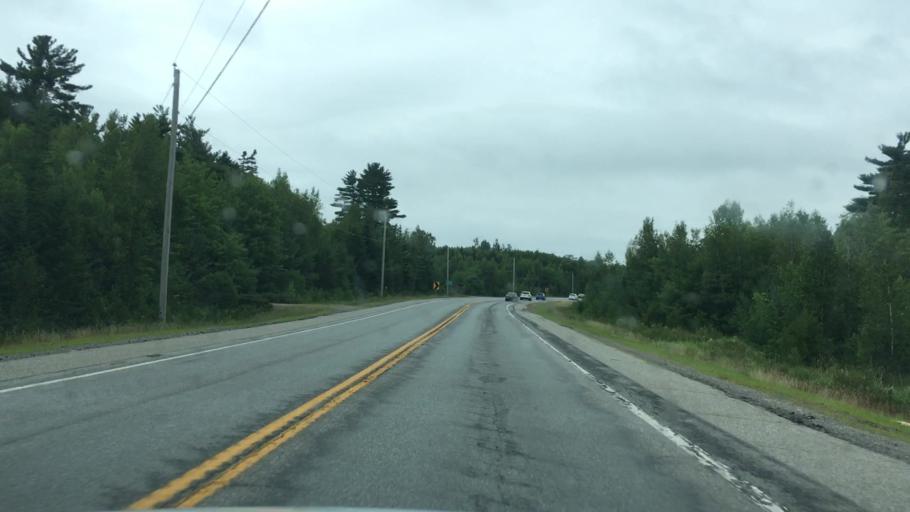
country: US
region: Maine
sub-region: Washington County
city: Cherryfield
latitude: 44.8515
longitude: -68.0598
